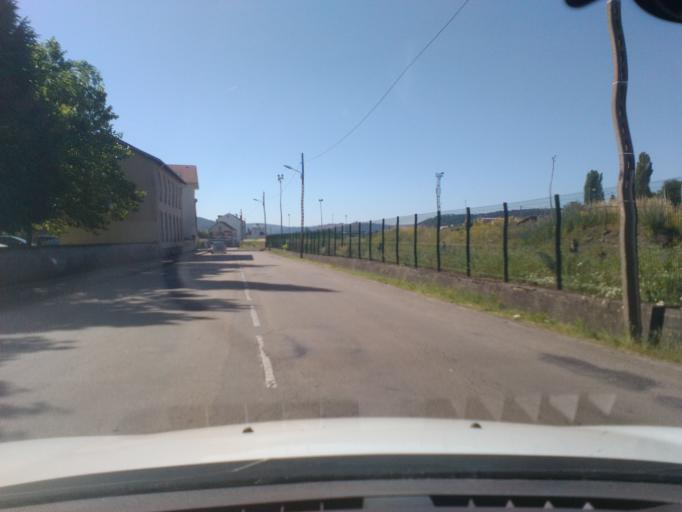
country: FR
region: Lorraine
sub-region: Departement des Vosges
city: Golbey
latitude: 48.1877
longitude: 6.4388
